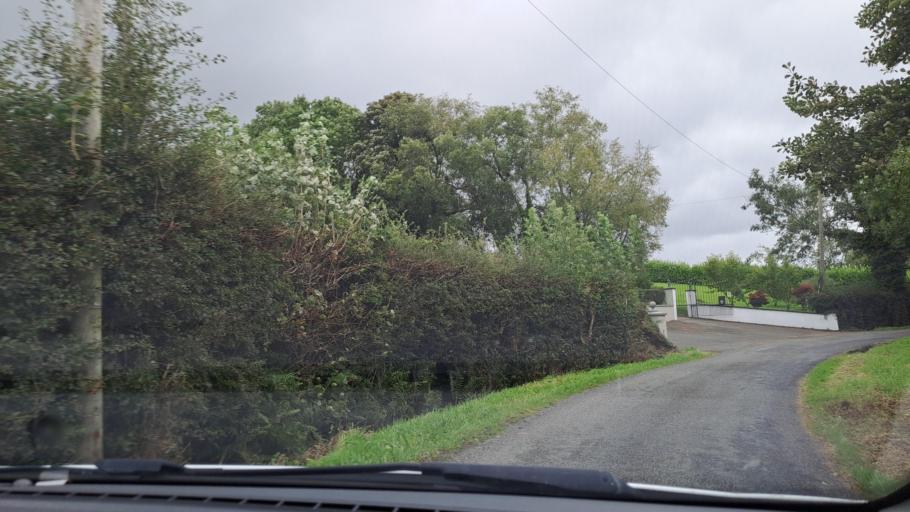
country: IE
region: Ulster
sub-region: An Cabhan
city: Kingscourt
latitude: 53.9735
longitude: -6.8638
